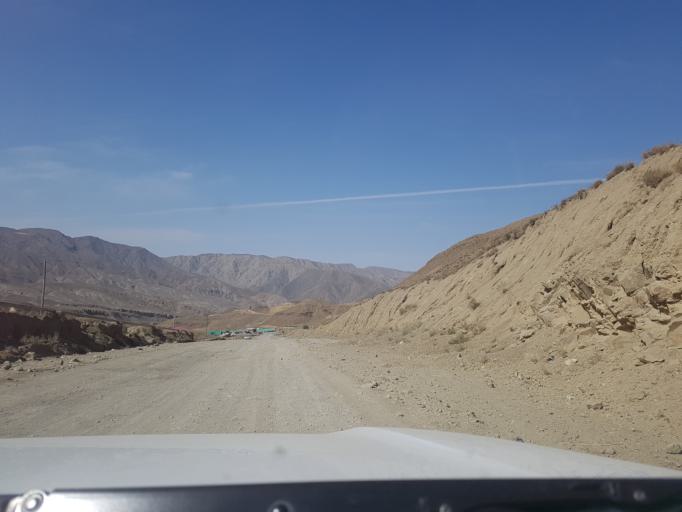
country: TM
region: Ahal
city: Baharly
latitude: 38.4493
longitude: 57.0475
